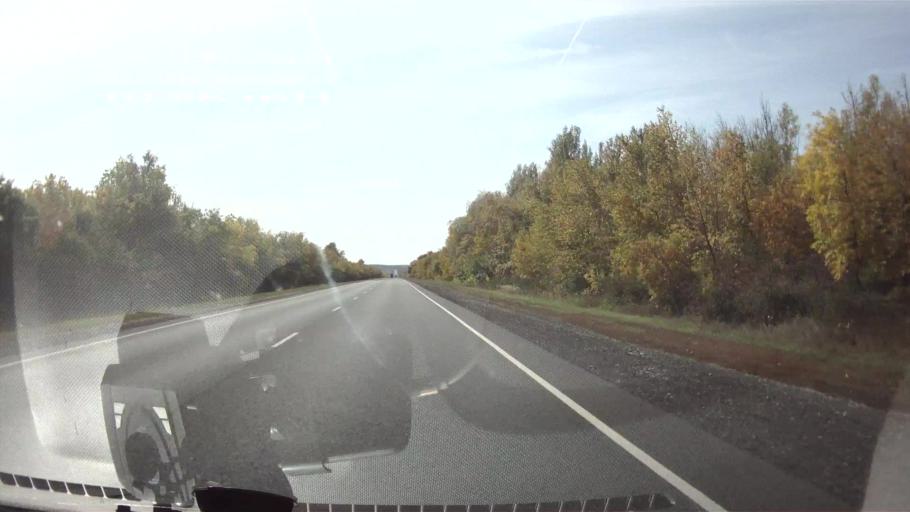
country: RU
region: Saratov
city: Khvalynsk
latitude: 52.5996
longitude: 48.1428
